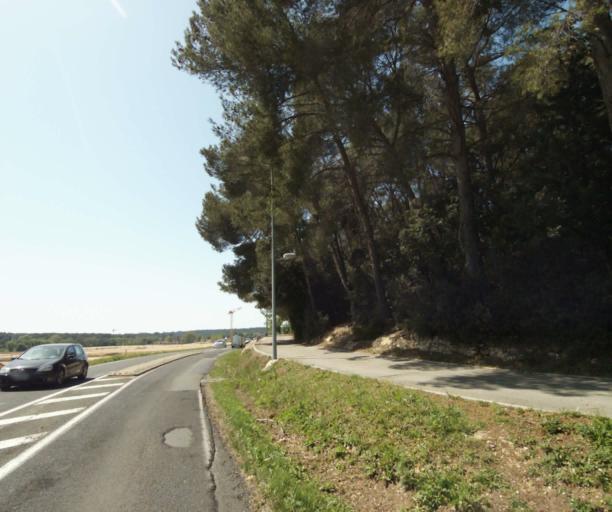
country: FR
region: Languedoc-Roussillon
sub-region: Departement de l'Herault
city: Clapiers
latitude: 43.6588
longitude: 3.8952
